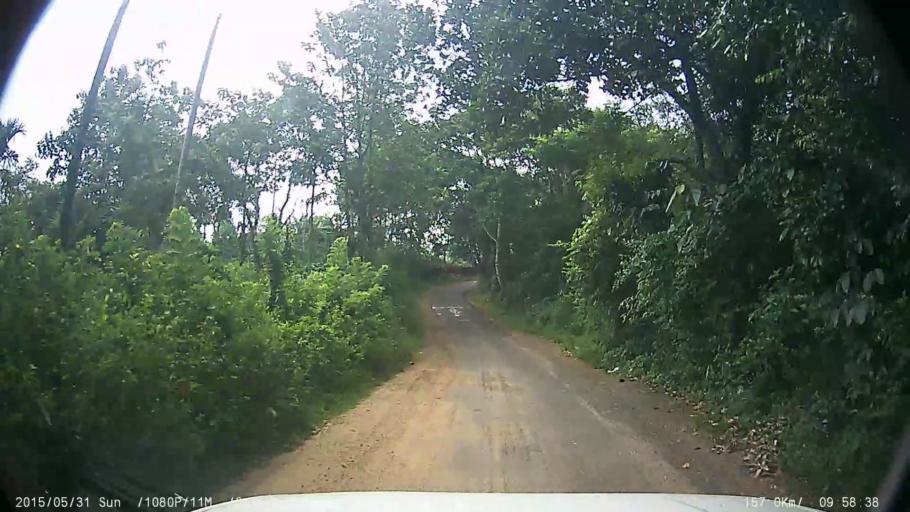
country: IN
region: Kerala
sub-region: Wayanad
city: Kalpetta
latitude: 11.5919
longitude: 76.0643
